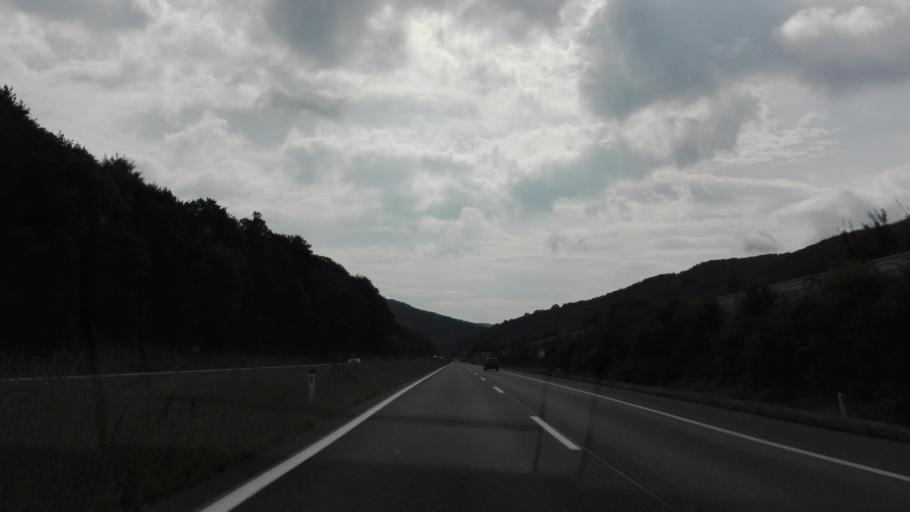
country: AT
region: Lower Austria
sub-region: Politischer Bezirk Baden
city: Klausen-Leopoldsdorf
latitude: 48.0842
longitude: 16.0295
